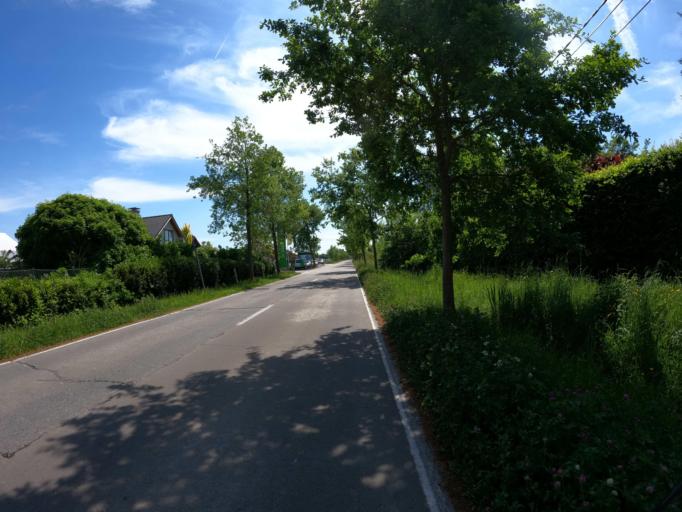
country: BE
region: Flanders
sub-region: Provincie Oost-Vlaanderen
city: Nazareth
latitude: 50.9769
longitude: 3.5690
